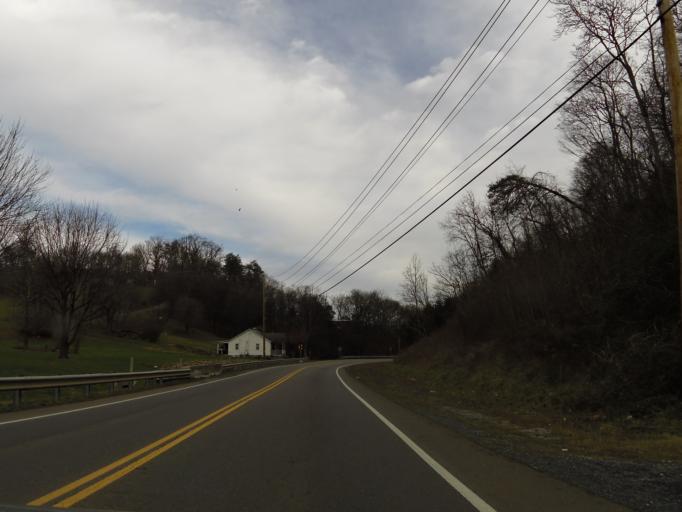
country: US
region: Tennessee
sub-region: Cocke County
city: Newport
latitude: 35.9789
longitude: -83.1683
